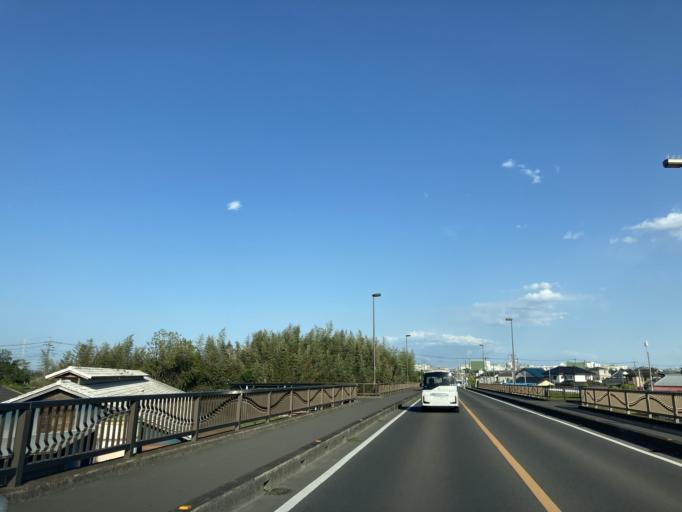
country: JP
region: Saitama
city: Sayama
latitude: 35.8856
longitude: 139.4194
